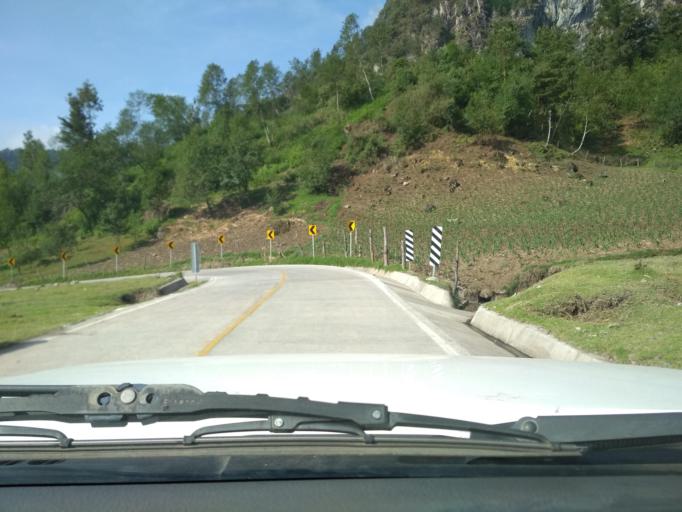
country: MX
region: Veracruz
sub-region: La Perla
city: Chilapa
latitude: 18.9976
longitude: -97.1871
